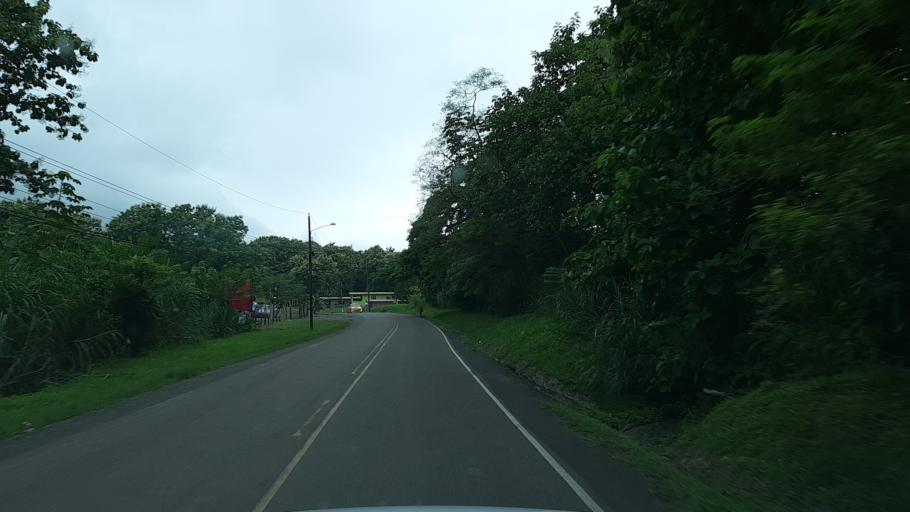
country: PA
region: Colon
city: Rio Duque
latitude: 9.2459
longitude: -79.6568
